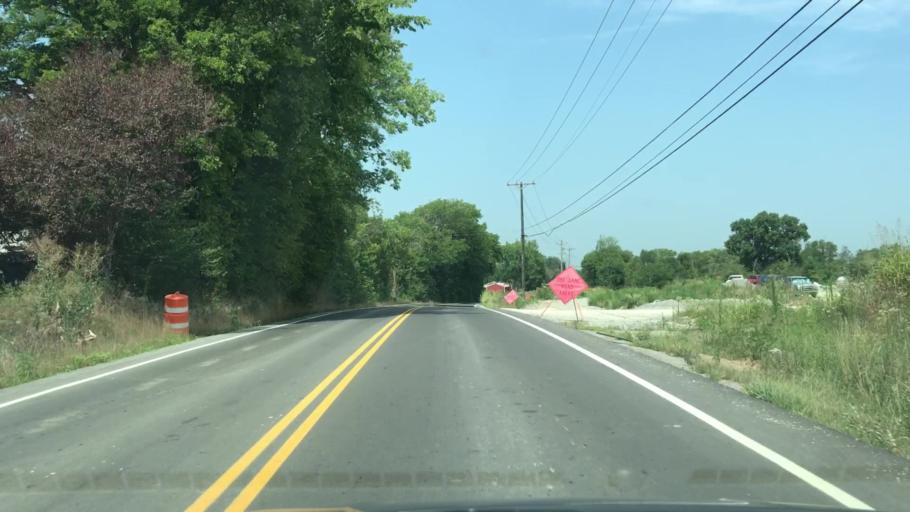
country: US
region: Tennessee
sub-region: Wilson County
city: Rural Hill
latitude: 36.1131
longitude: -86.4286
